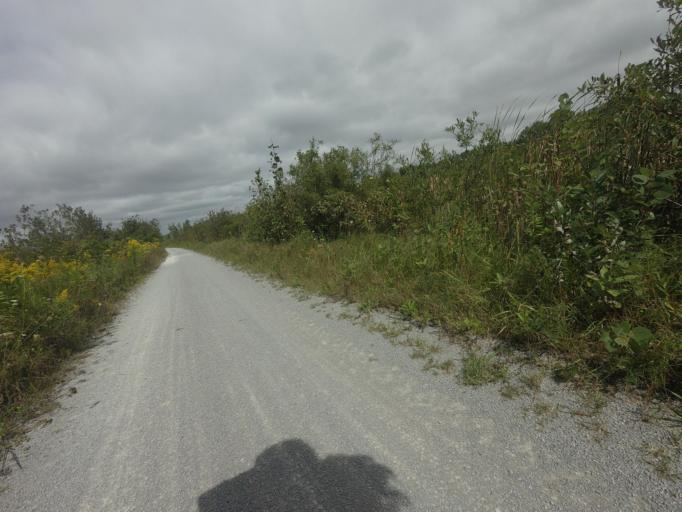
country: CA
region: Ontario
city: Uxbridge
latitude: 44.1985
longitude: -79.0619
